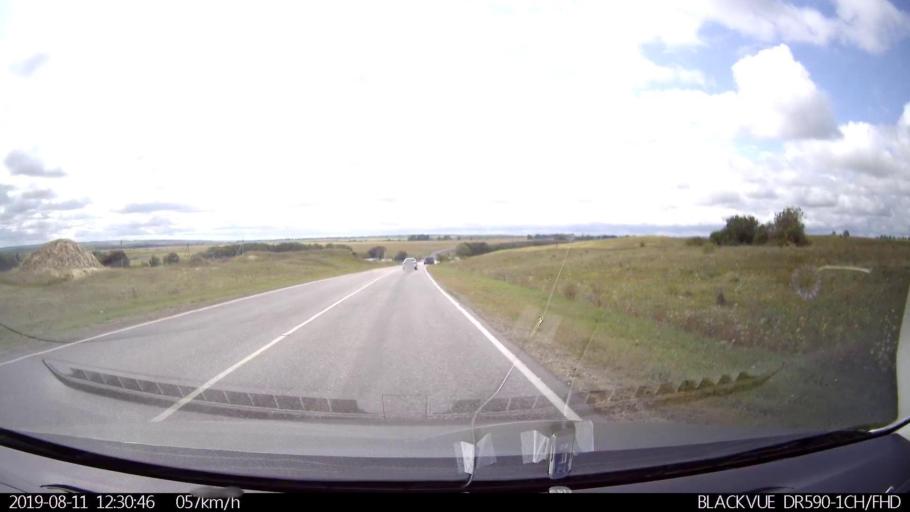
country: RU
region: Ulyanovsk
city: Ignatovka
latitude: 53.8237
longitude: 47.8913
